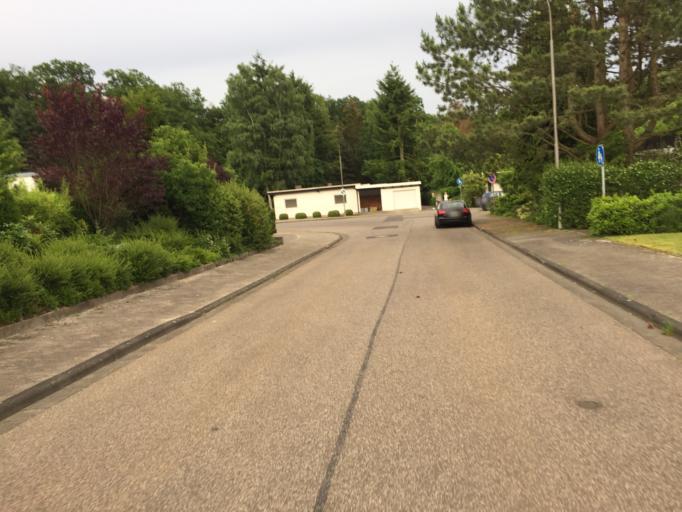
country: DE
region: Hesse
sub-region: Regierungsbezirk Giessen
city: Giessen
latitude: 50.5459
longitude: 8.7237
